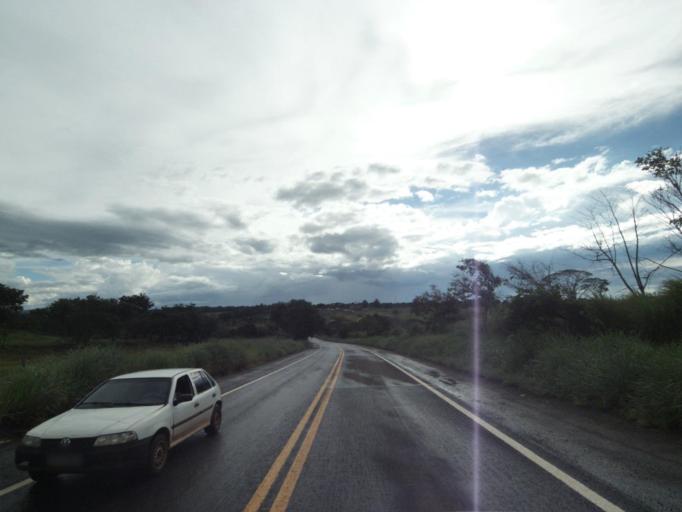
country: BR
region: Goias
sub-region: Itaberai
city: Itaberai
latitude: -15.9138
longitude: -49.5891
